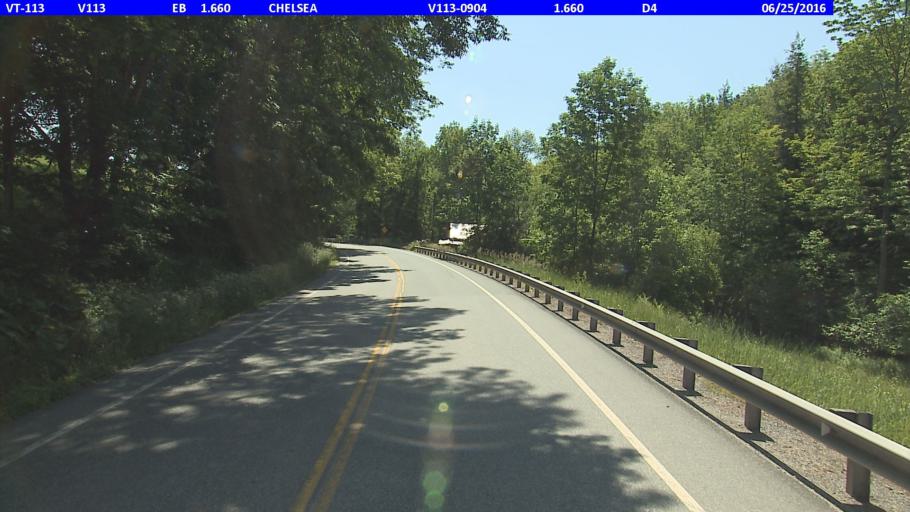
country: US
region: Vermont
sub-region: Orange County
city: Chelsea
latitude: 43.9894
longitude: -72.4190
